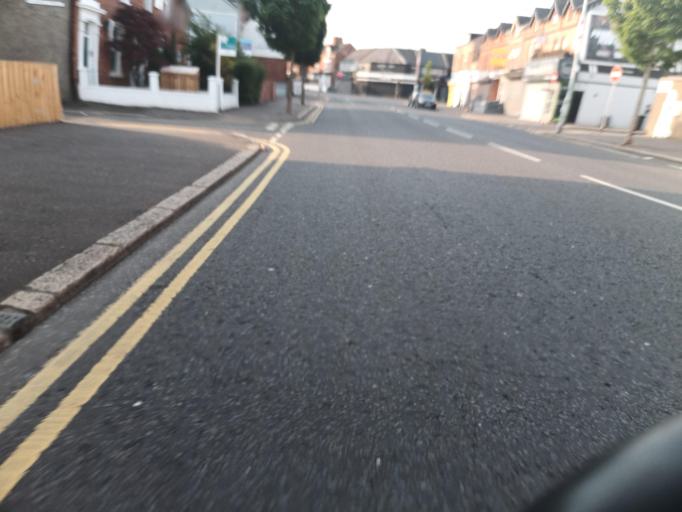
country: GB
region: Northern Ireland
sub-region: Castlereagh District
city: Castlereagh
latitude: 54.5944
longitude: -5.8874
